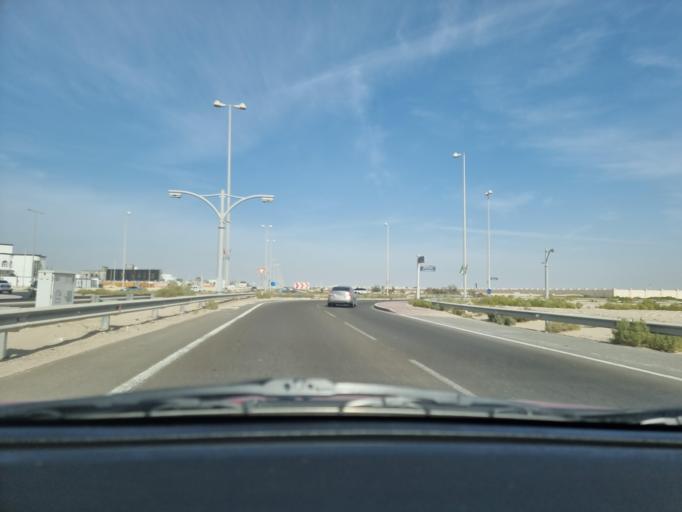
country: AE
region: Abu Dhabi
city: Abu Dhabi
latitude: 24.3749
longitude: 54.6741
